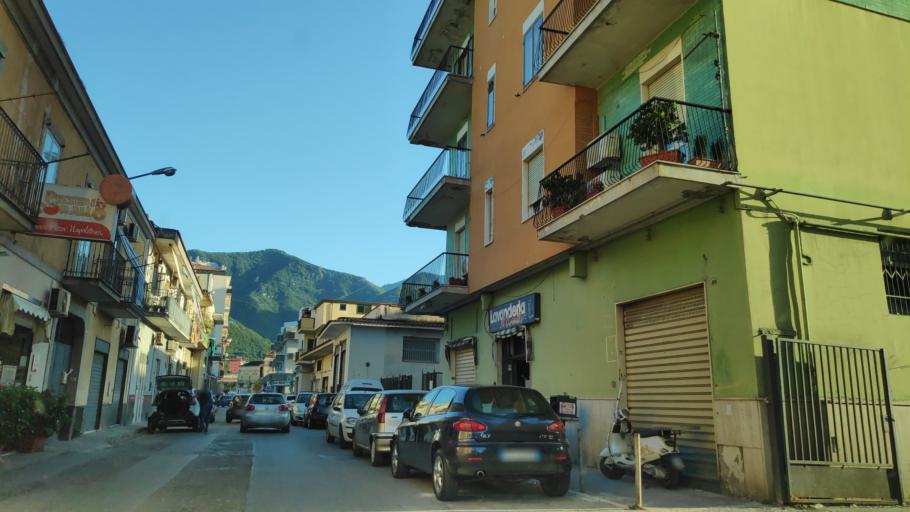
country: IT
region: Campania
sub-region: Provincia di Salerno
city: Pagani
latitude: 40.7492
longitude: 14.6148
